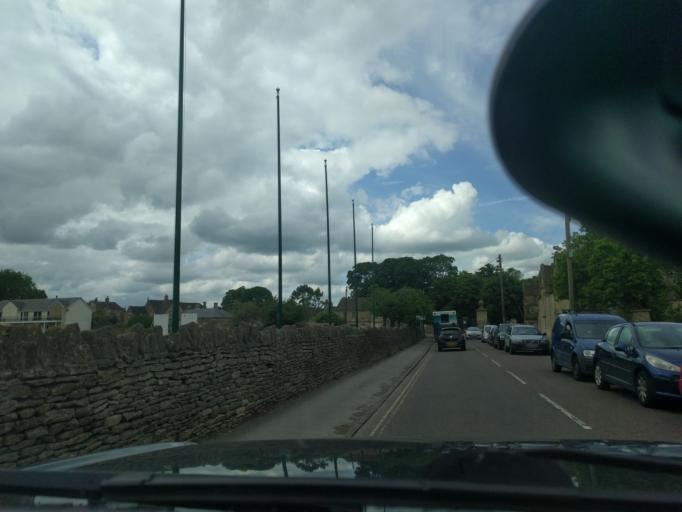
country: GB
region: England
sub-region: Wiltshire
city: Corsham
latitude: 51.4297
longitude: -2.1841
